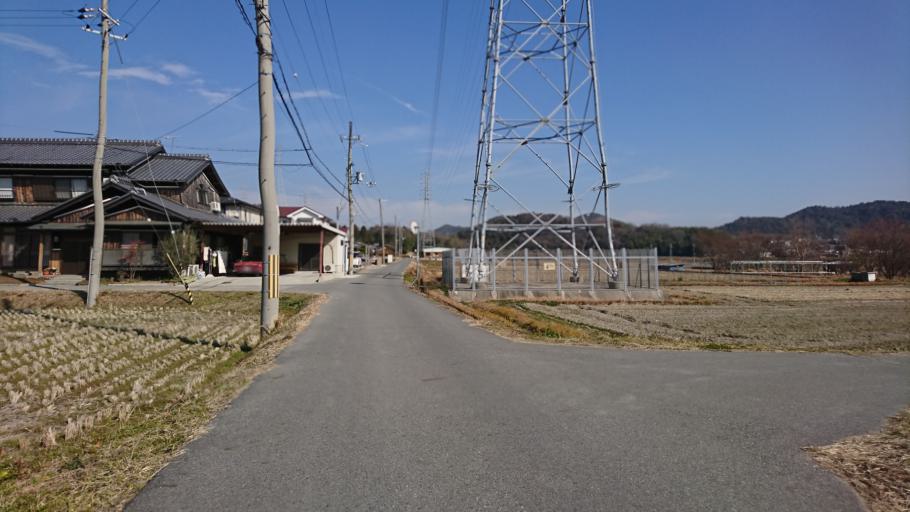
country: JP
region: Hyogo
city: Kakogawacho-honmachi
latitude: 34.8058
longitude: 134.8614
